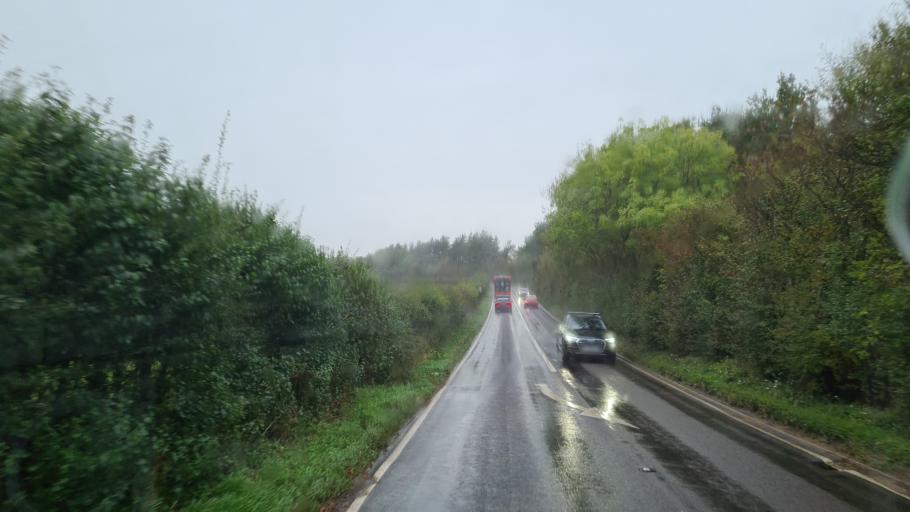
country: GB
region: England
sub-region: West Sussex
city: Washington
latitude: 50.9092
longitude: -0.3887
